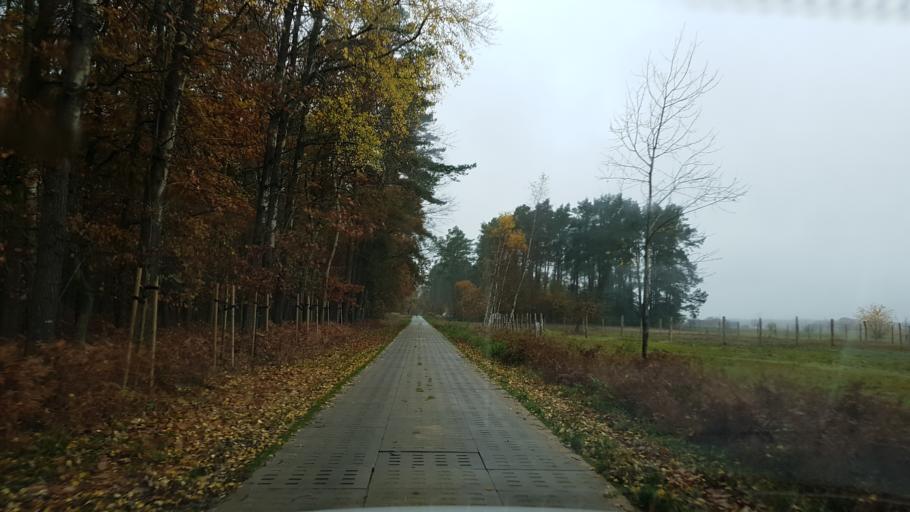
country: PL
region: West Pomeranian Voivodeship
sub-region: Powiat goleniowski
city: Goleniow
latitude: 53.5783
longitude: 14.7954
